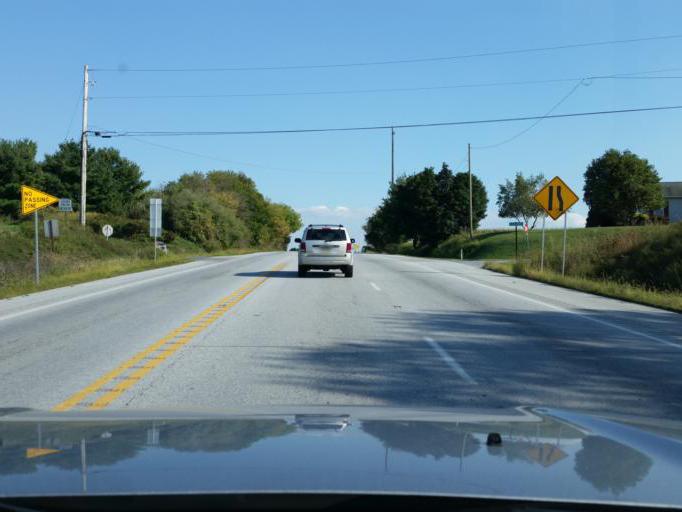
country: US
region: Pennsylvania
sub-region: Chester County
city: Atglen
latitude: 39.9355
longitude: -75.9567
